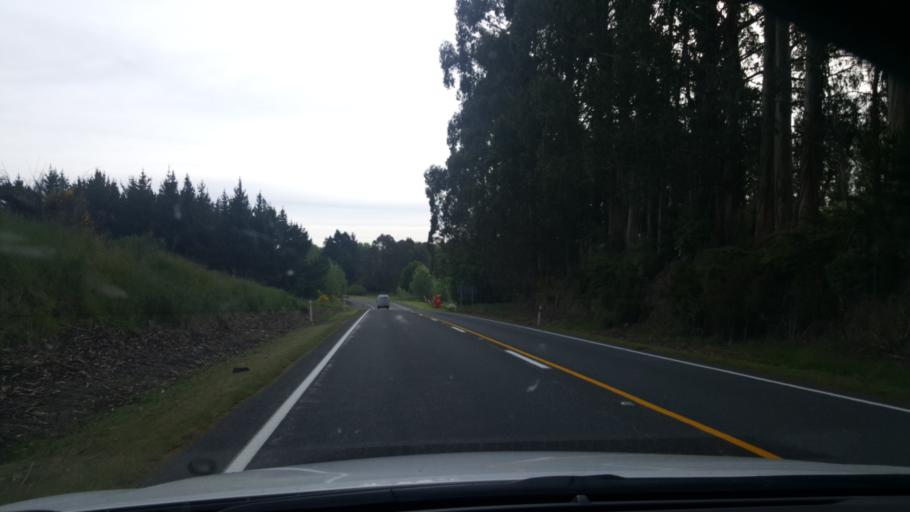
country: NZ
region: Waikato
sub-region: Taupo District
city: Taupo
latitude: -38.6146
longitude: 176.1149
